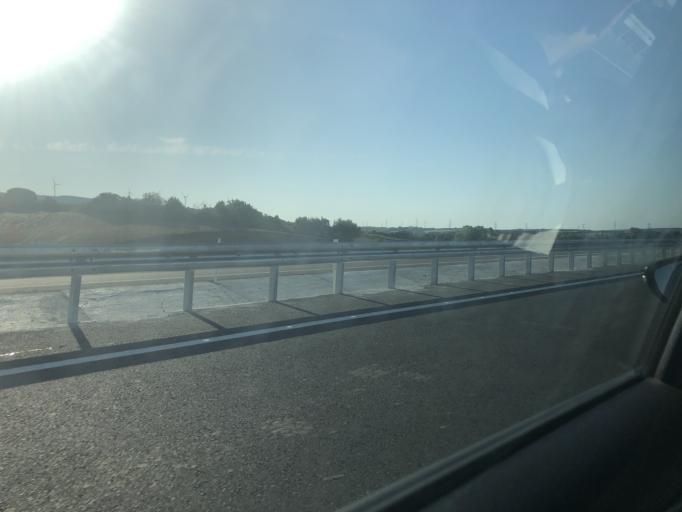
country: TR
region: Istanbul
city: Catalca
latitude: 41.1584
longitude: 28.4642
